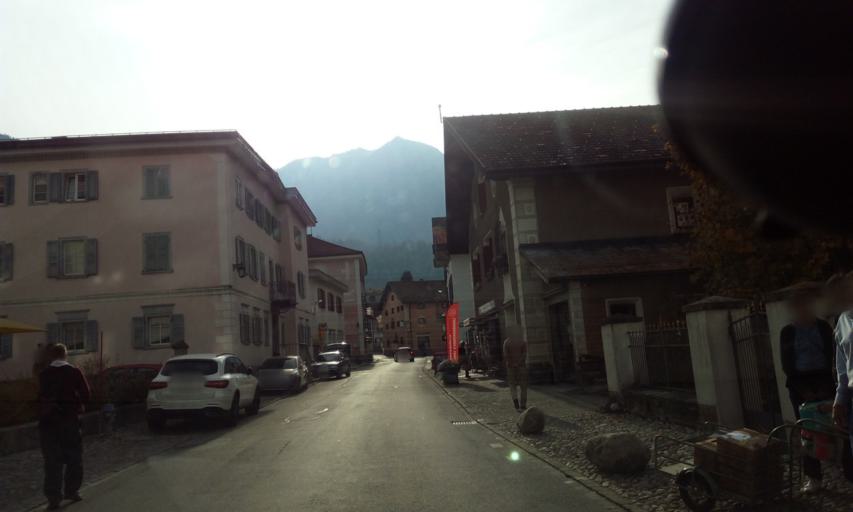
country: CH
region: Grisons
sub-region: Maloja District
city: Samedan
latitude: 46.6289
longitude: 9.7455
